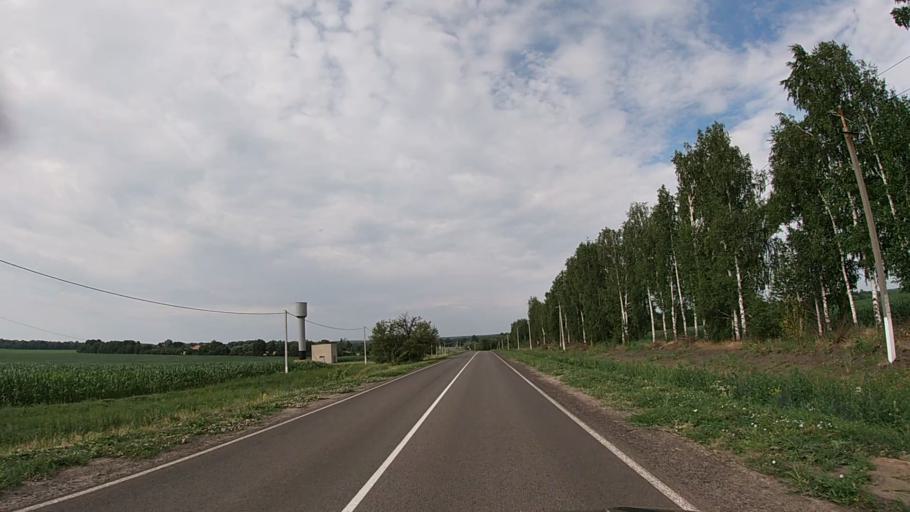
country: UA
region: Sumy
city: Krasnopillya
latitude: 50.8175
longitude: 35.4509
